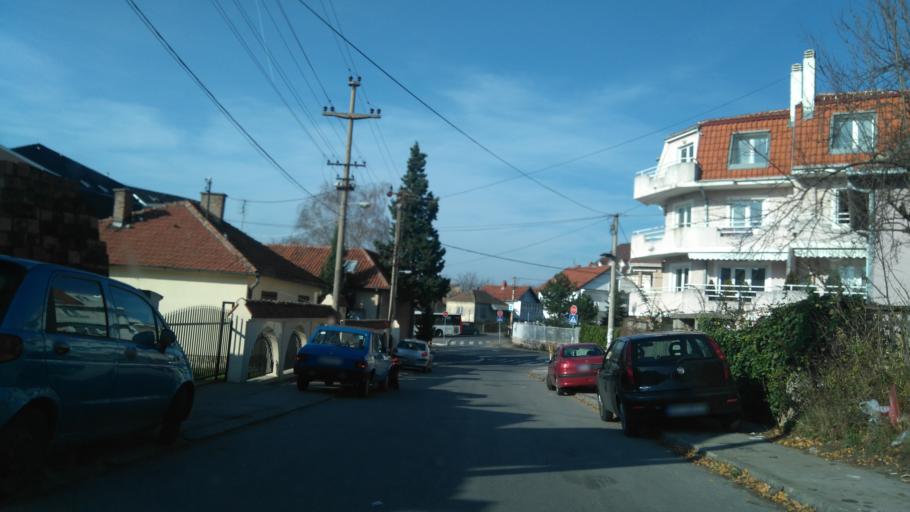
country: RS
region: Central Serbia
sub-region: Belgrade
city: Cukarica
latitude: 44.7588
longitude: 20.4071
